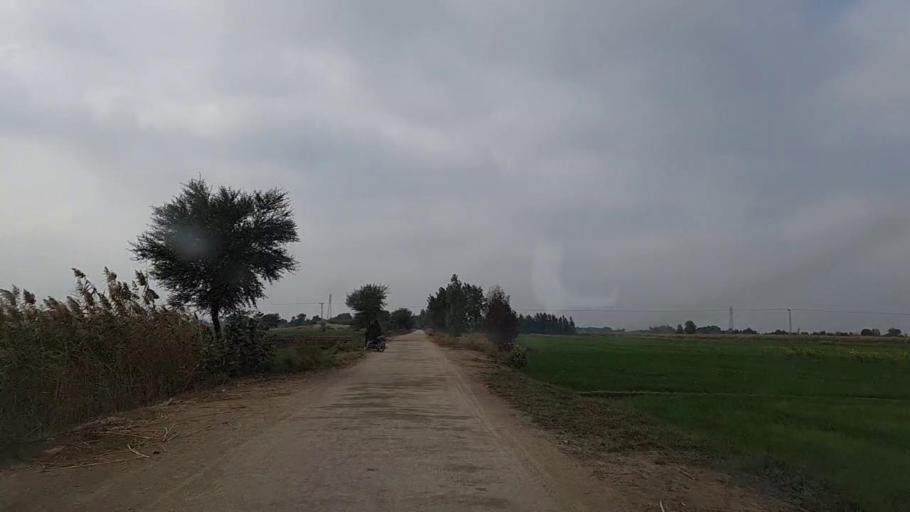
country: PK
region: Sindh
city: Sanghar
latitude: 26.1741
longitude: 68.9565
